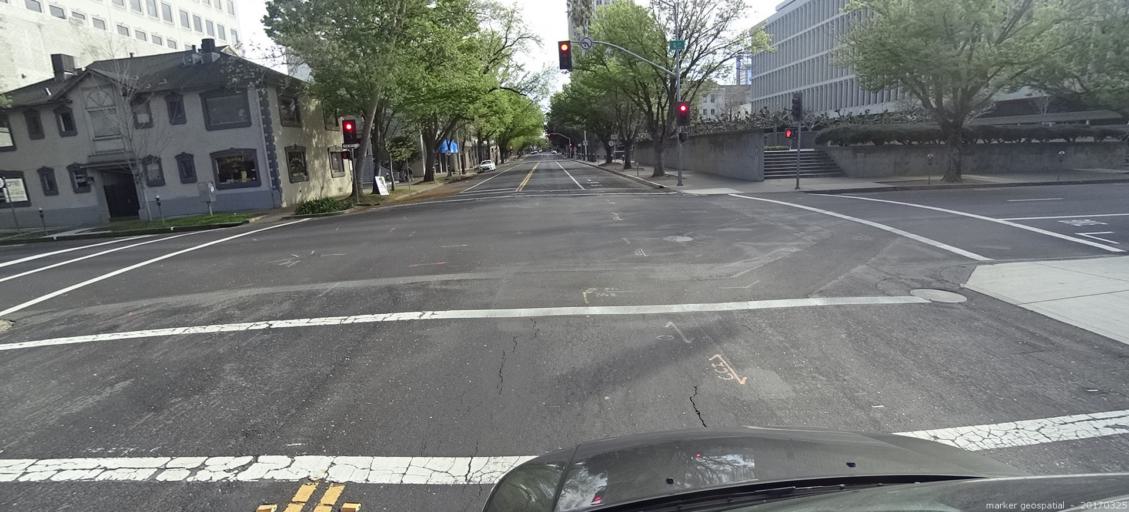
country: US
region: California
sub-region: Sacramento County
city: Sacramento
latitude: 38.5841
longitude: -121.4934
